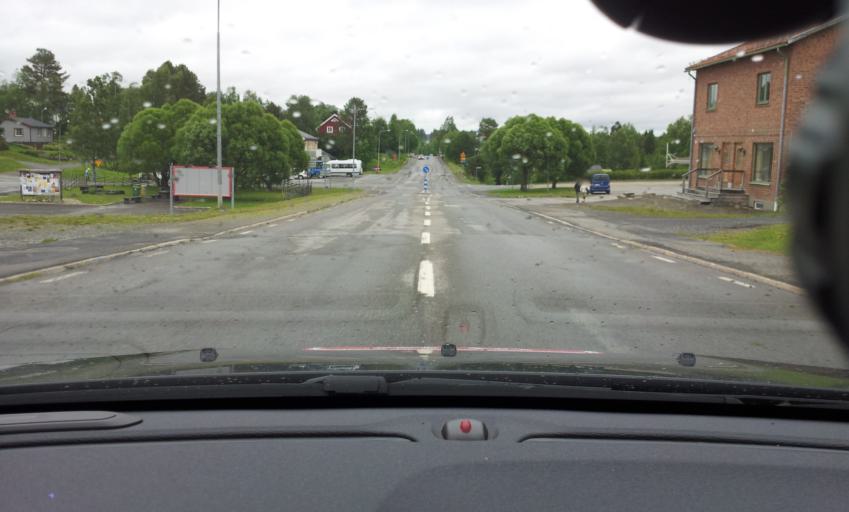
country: SE
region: Jaemtland
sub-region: Krokoms Kommun
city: Krokom
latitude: 63.6702
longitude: 14.6105
